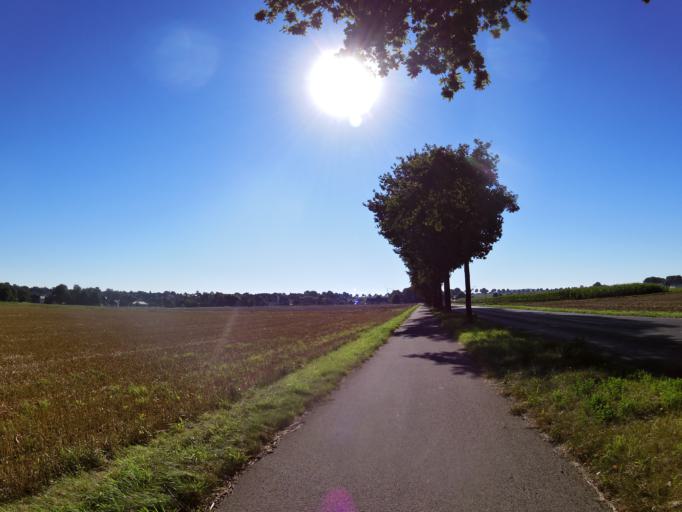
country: DE
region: North Rhine-Westphalia
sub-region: Regierungsbezirk Koln
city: Ubach-Palenberg
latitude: 50.9514
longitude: 6.0682
